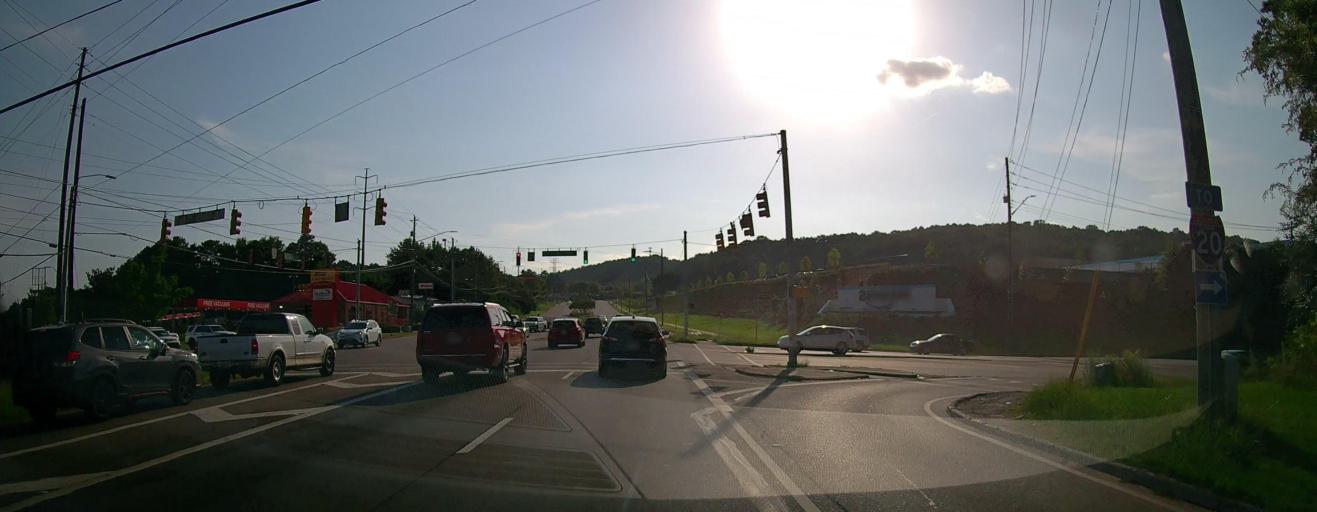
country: US
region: Alabama
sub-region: Jefferson County
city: Irondale
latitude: 33.5307
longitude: -86.7206
